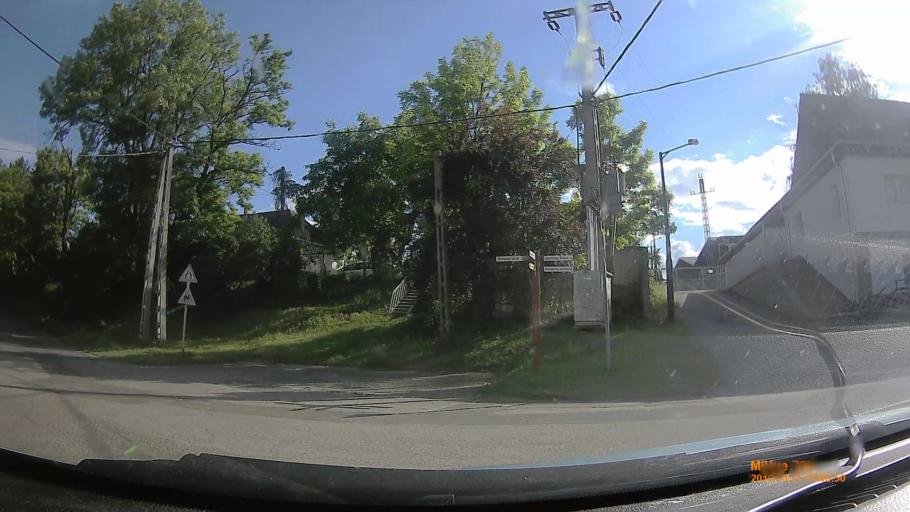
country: HU
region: Nograd
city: Nagyoroszi
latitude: 48.0474
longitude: 19.0533
